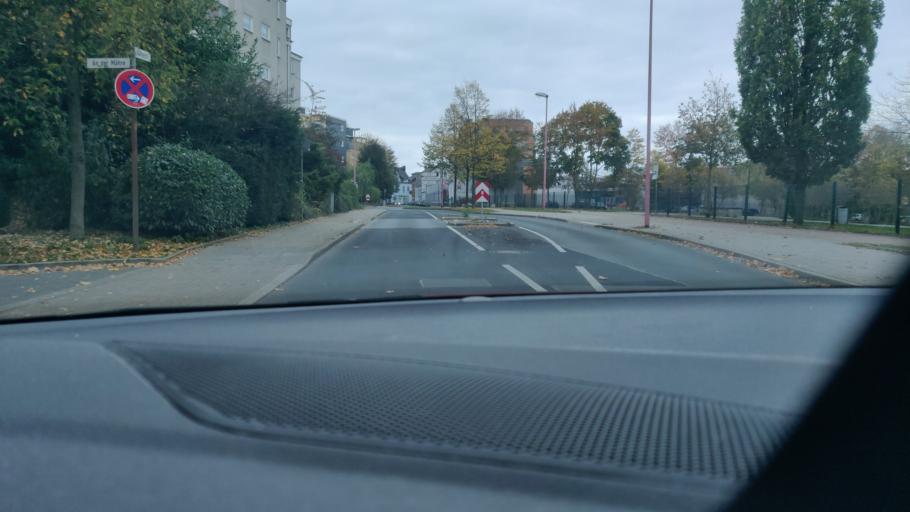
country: DE
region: North Rhine-Westphalia
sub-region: Regierungsbezirk Dusseldorf
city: Velbert
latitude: 51.3437
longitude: 7.0492
